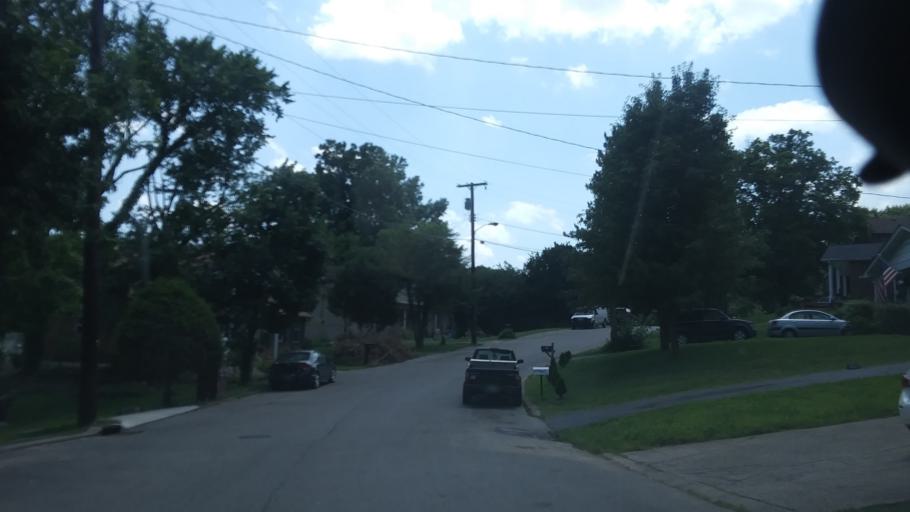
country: US
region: Tennessee
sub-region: Davidson County
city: Oak Hill
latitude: 36.0825
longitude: -86.7068
